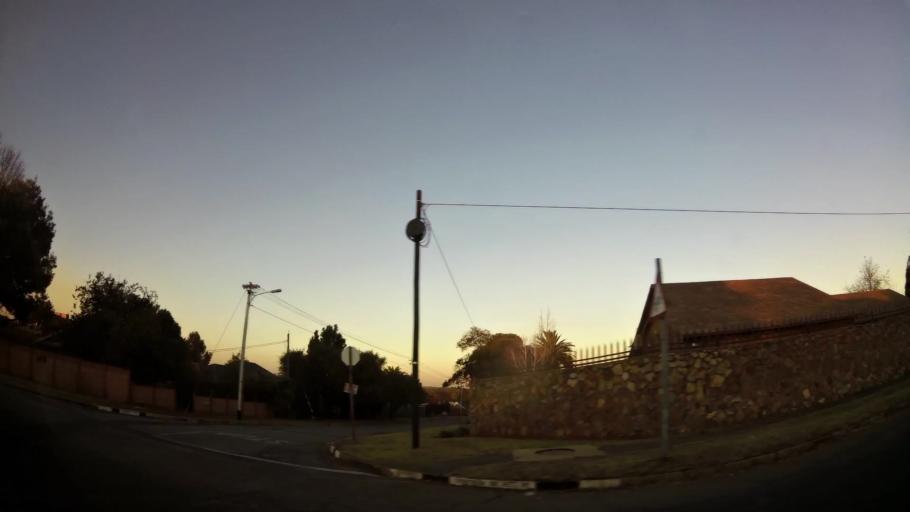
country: ZA
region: Gauteng
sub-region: City of Johannesburg Metropolitan Municipality
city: Roodepoort
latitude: -26.1604
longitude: 27.9000
